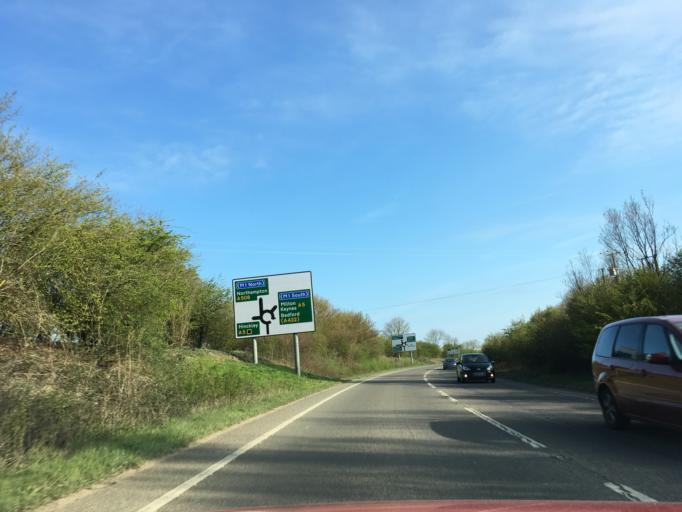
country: GB
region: England
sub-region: Northamptonshire
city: Deanshanger
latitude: 52.0632
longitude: -0.8721
